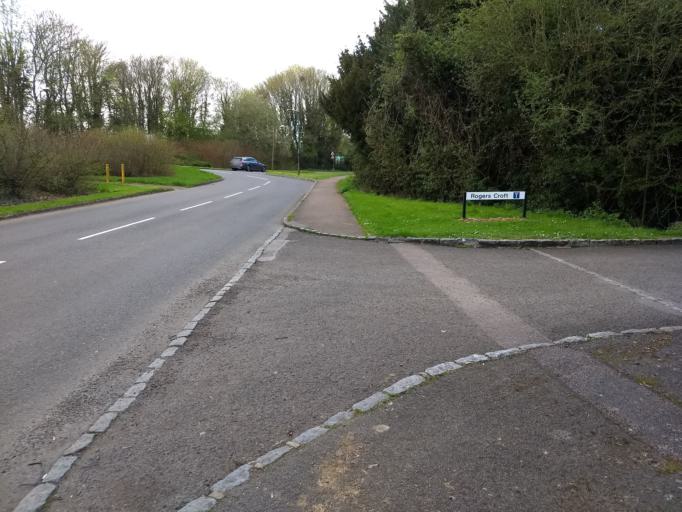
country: GB
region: England
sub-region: Milton Keynes
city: Simpson
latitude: 52.0263
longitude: -0.7215
